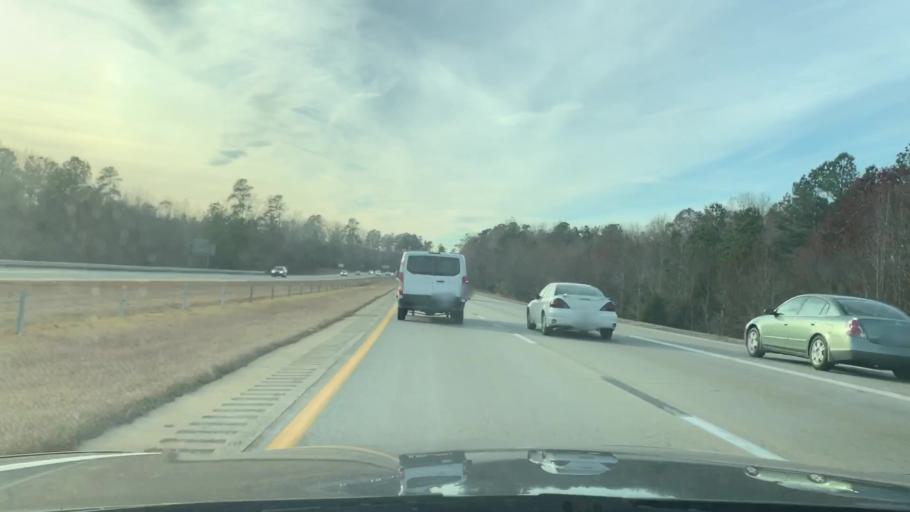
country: US
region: North Carolina
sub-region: Orange County
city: Hillsborough
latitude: 36.0378
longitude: -79.1014
